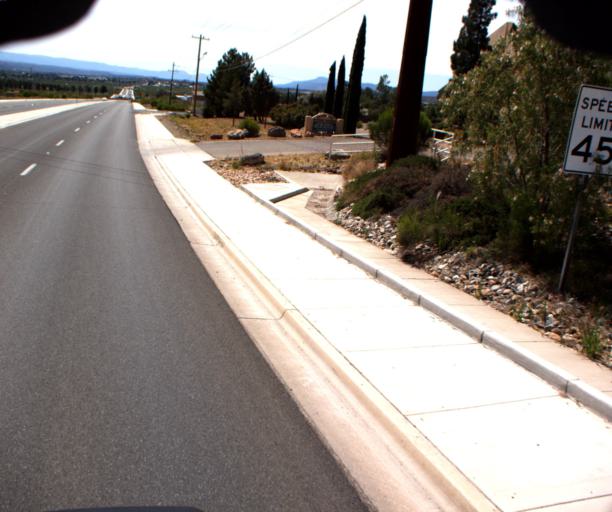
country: US
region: Arizona
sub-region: Yavapai County
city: Clarkdale
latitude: 34.7579
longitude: -112.0582
